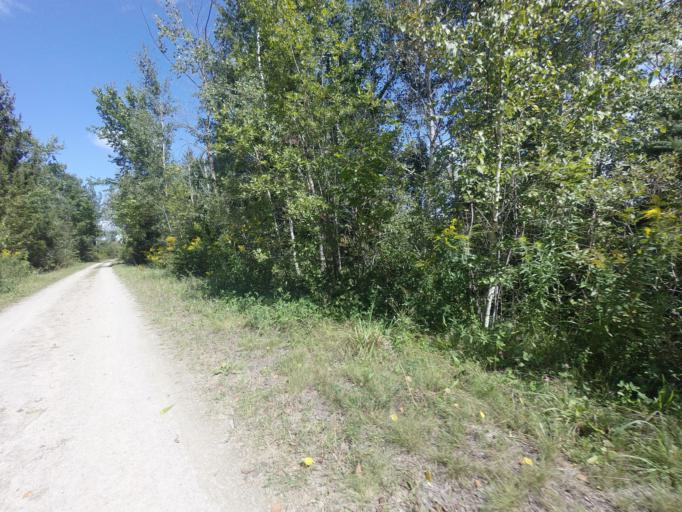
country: CA
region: Ontario
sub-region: Wellington County
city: Guelph
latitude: 43.7618
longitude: -80.3248
